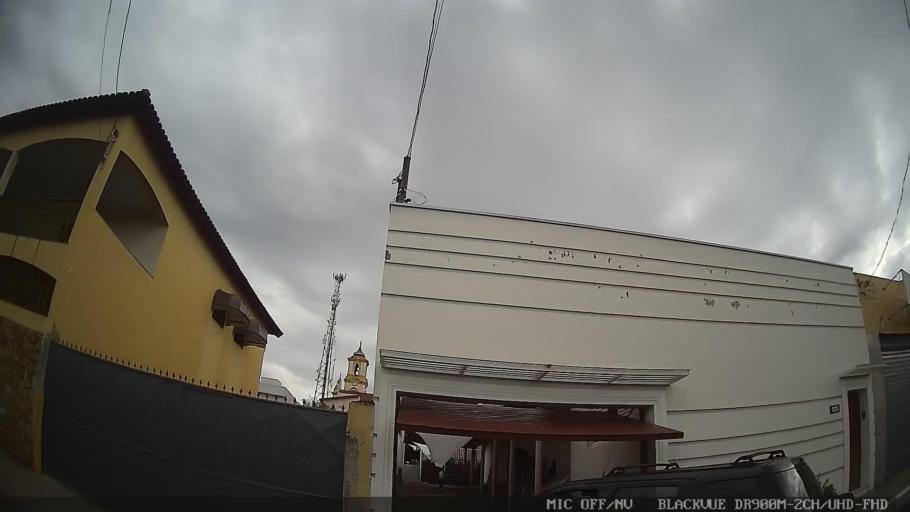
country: BR
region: Sao Paulo
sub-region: Salto
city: Salto
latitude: -23.2018
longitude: -47.2867
